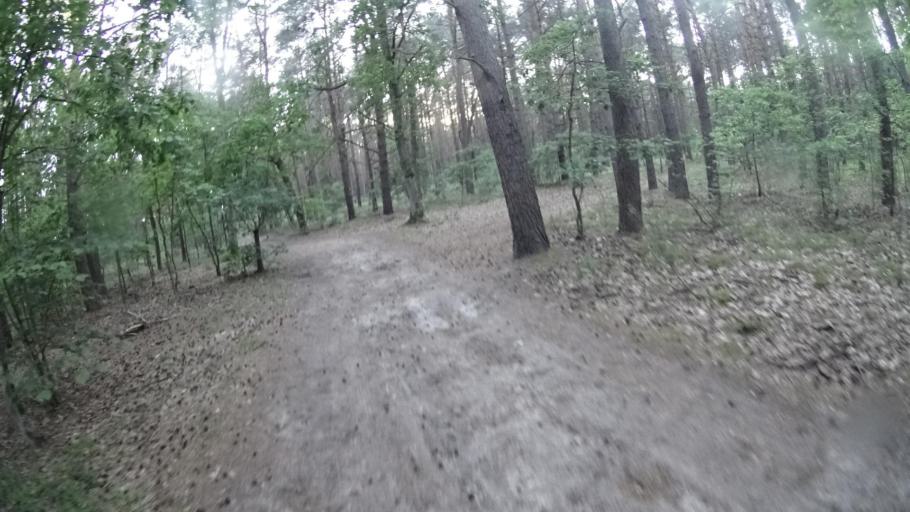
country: PL
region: Masovian Voivodeship
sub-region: Powiat warszawski zachodni
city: Truskaw
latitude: 52.2764
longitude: 20.7824
